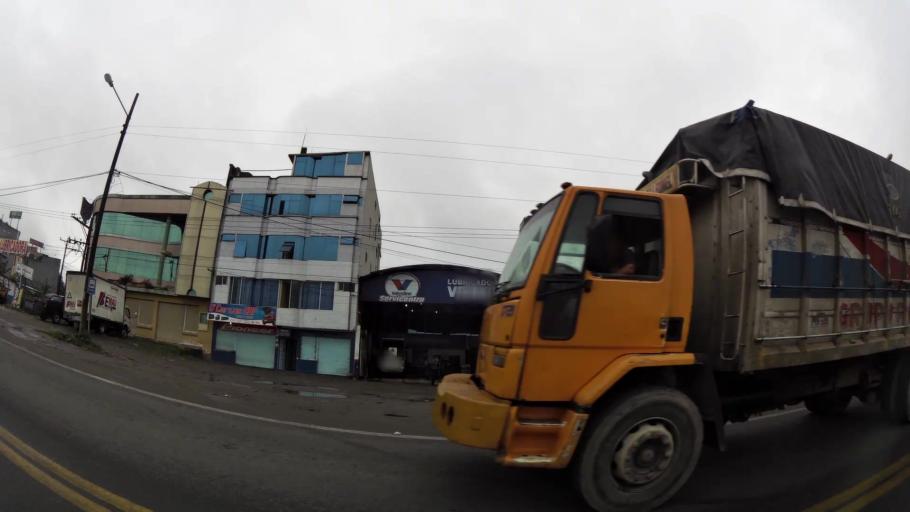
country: EC
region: Santo Domingo de los Tsachilas
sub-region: Canton Santo Domingo de los Colorados
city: Santo Domingo de los Colorados
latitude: -0.2375
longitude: -79.1734
